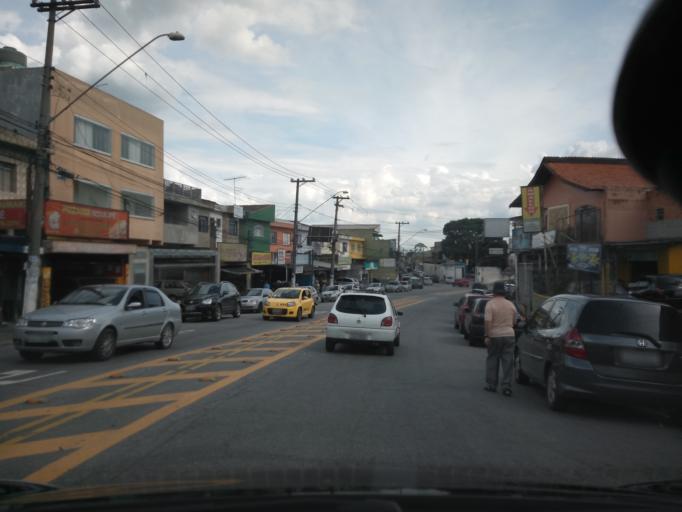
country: BR
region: Sao Paulo
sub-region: Sao Bernardo Do Campo
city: Sao Bernardo do Campo
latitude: -23.7393
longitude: -46.5695
